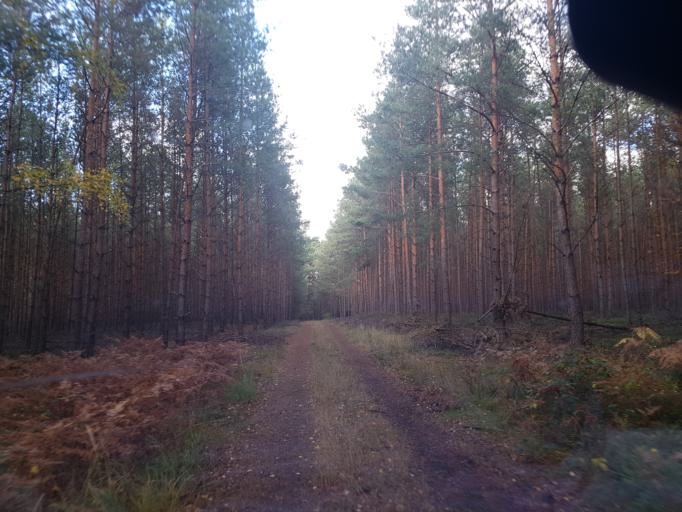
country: DE
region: Brandenburg
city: Finsterwalde
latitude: 51.5638
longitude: 13.7002
